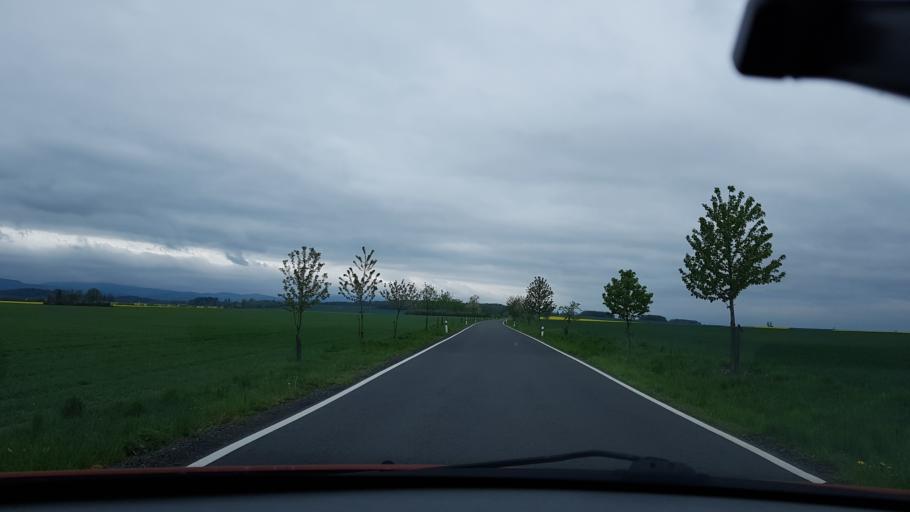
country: CZ
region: Olomoucky
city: Vidnava
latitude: 50.3781
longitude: 17.1681
